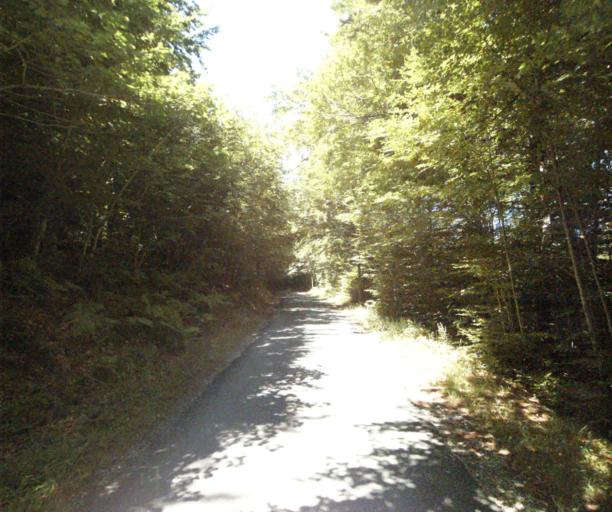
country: FR
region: Languedoc-Roussillon
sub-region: Departement de l'Aude
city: Cuxac-Cabardes
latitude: 43.4006
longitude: 2.2162
